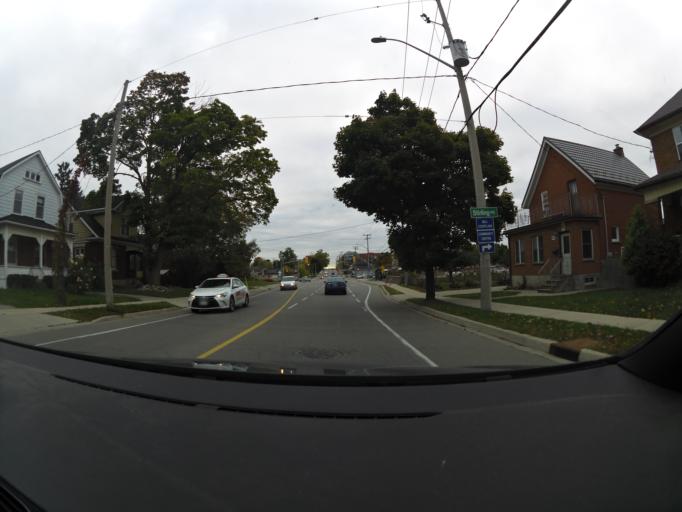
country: CA
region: Ontario
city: Kitchener
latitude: 43.4418
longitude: -80.4854
